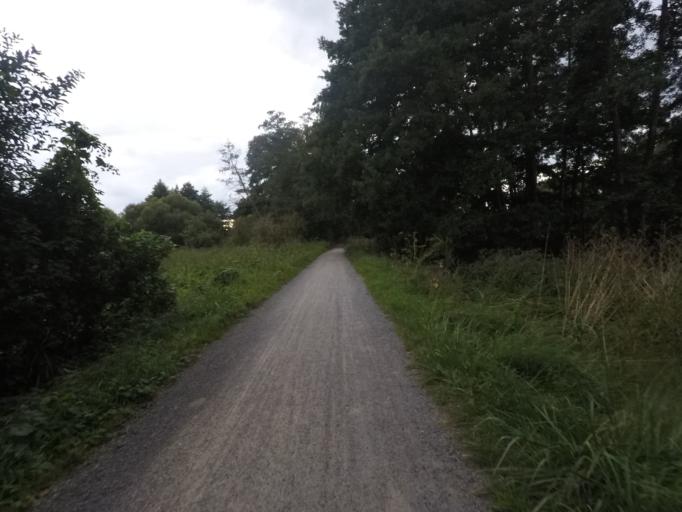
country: DE
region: North Rhine-Westphalia
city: Bad Oeynhausen
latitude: 52.2078
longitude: 8.7751
